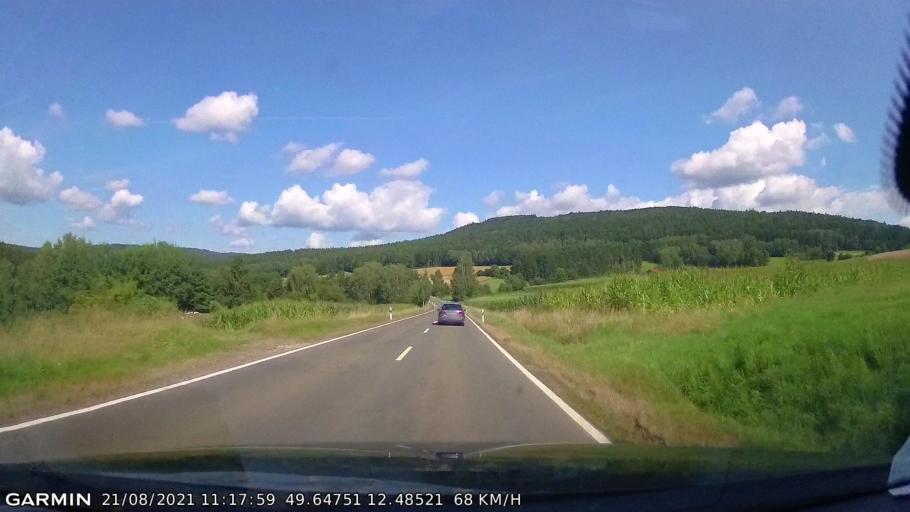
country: DE
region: Bavaria
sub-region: Upper Palatinate
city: Waidhaus
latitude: 49.6477
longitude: 12.4852
